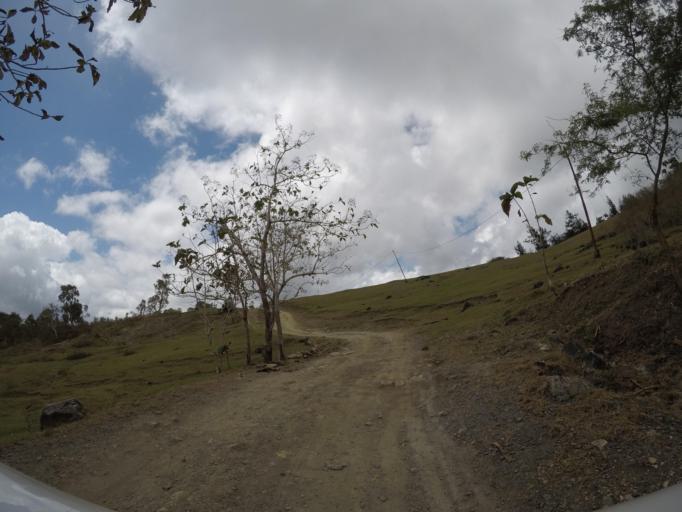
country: TL
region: Lautem
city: Lospalos
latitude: -8.5563
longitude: 126.8324
